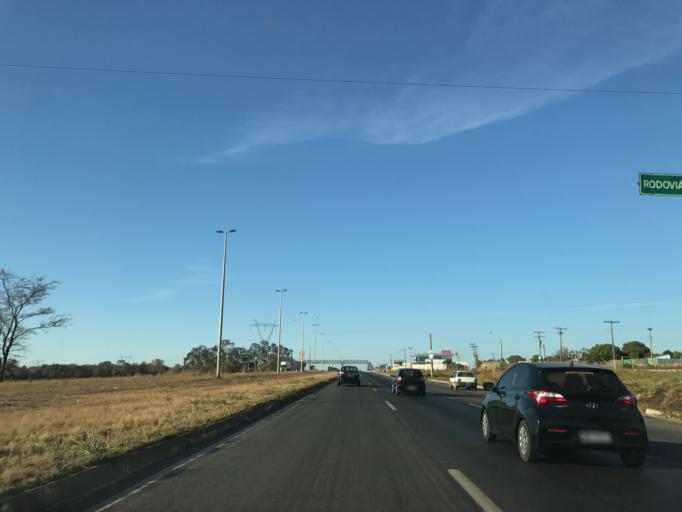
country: BR
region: Goias
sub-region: Aparecida De Goiania
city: Aparecida de Goiania
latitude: -16.8333
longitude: -49.2438
